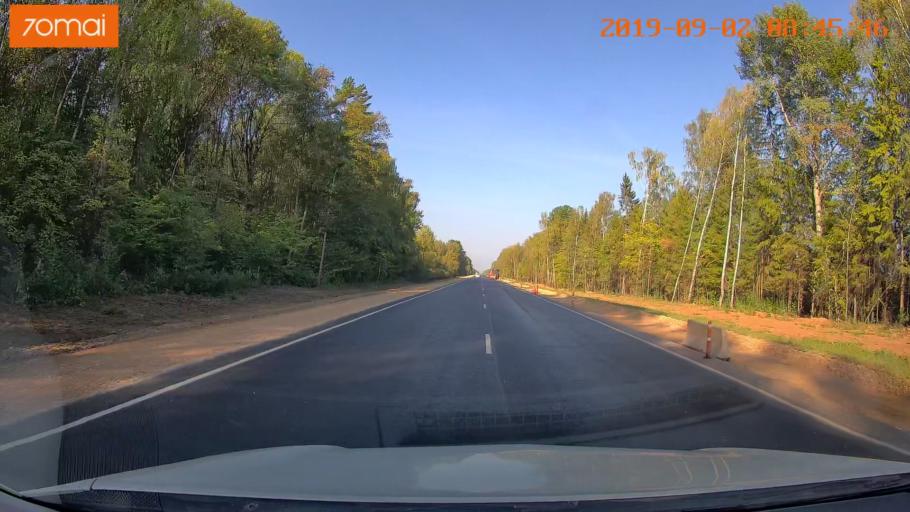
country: RU
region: Kaluga
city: Medyn'
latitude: 54.9693
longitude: 35.9961
